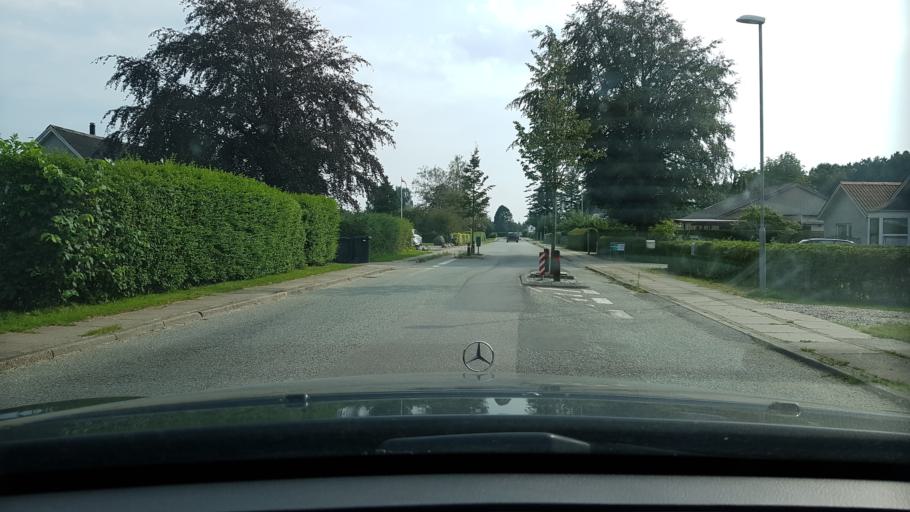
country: DK
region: North Denmark
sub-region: Alborg Kommune
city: Hals
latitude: 56.9730
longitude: 10.2170
